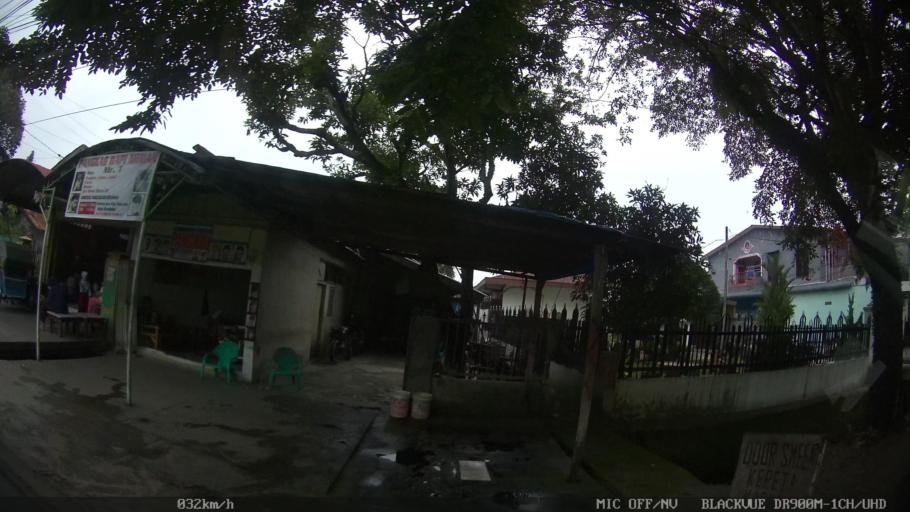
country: ID
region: North Sumatra
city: Deli Tua
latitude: 3.5523
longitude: 98.7102
